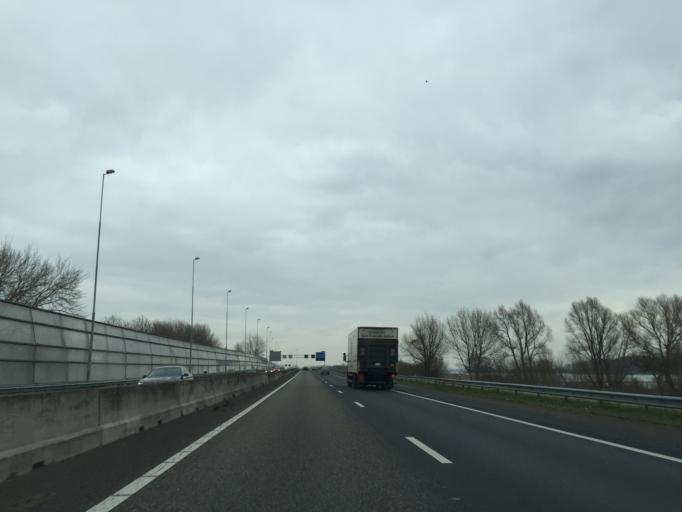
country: NL
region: South Holland
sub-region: Gemeente Hardinxveld-Giessendam
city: Neder-Hardinxveld
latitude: 51.8214
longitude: 4.8226
